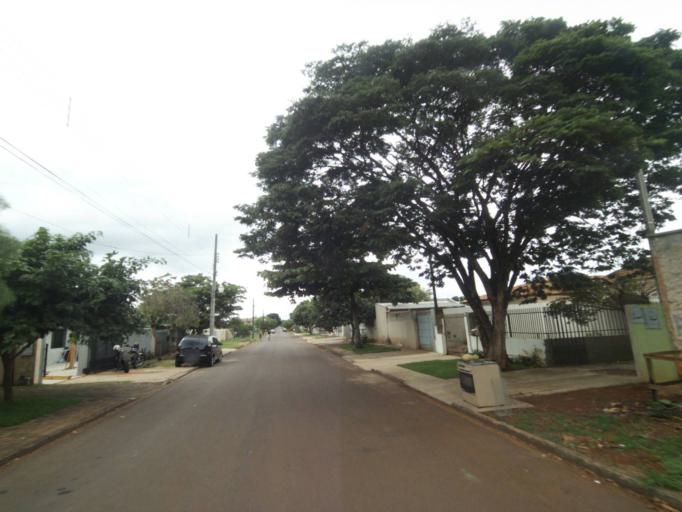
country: BR
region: Parana
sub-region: Campo Mourao
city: Campo Mourao
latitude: -24.0210
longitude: -52.3573
